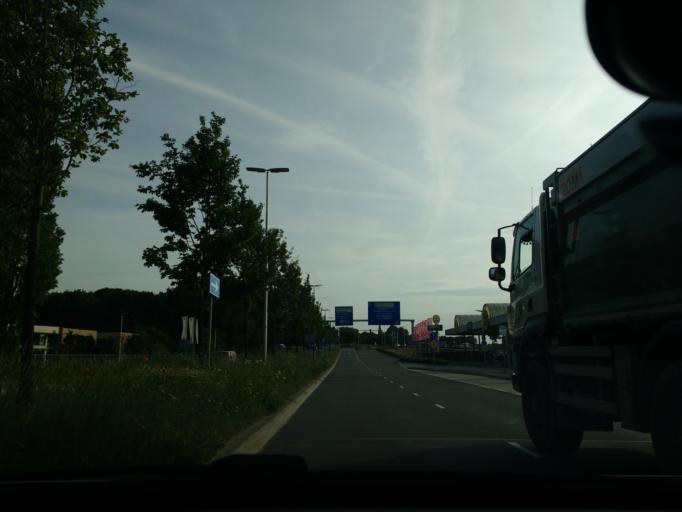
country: NL
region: Gelderland
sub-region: Gemeente Nijmegen
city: Lindenholt
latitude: 51.8381
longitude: 5.8170
